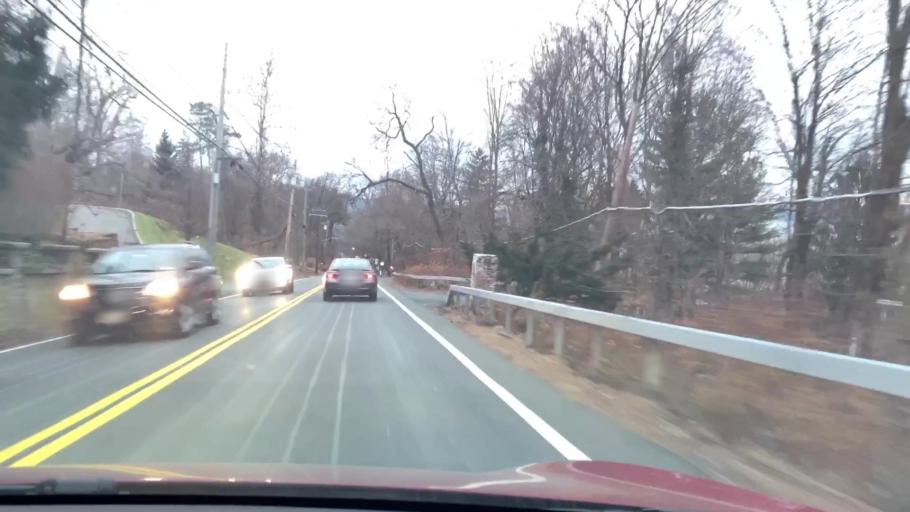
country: US
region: New York
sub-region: Rockland County
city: South Nyack
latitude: 41.0692
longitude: -73.9232
